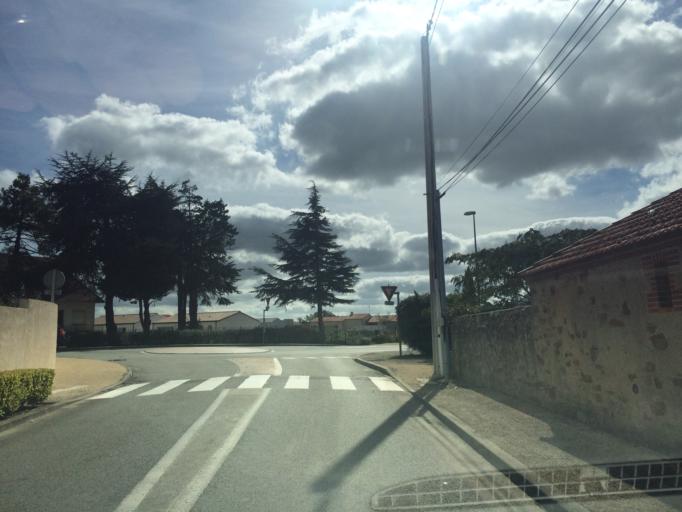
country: FR
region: Pays de la Loire
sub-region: Departement de la Loire-Atlantique
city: Chemere
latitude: 47.1203
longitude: -1.9217
